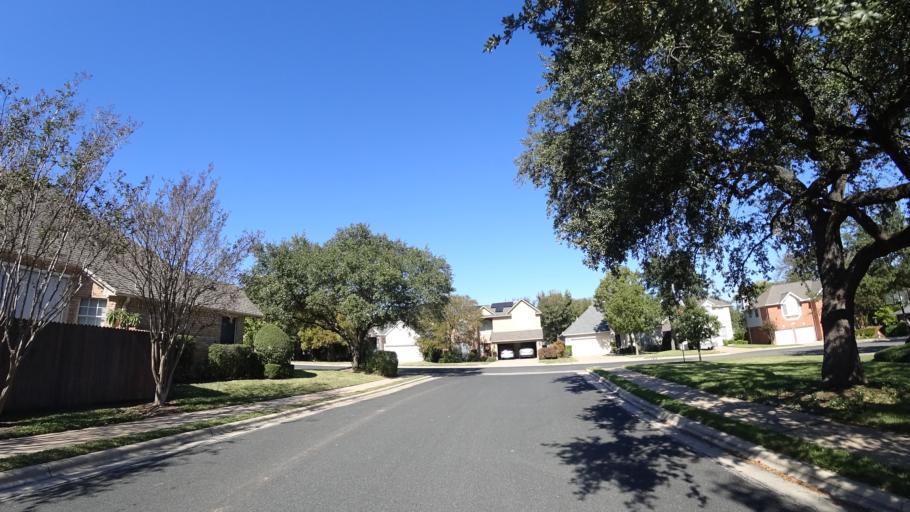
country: US
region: Texas
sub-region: Williamson County
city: Jollyville
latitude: 30.3832
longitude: -97.7458
